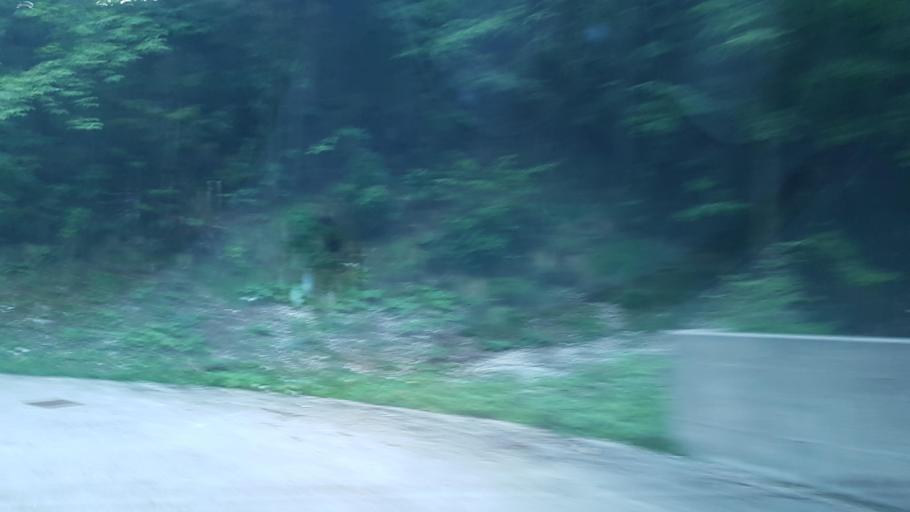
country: IT
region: Friuli Venezia Giulia
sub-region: Provincia di Udine
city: Malborghetto
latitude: 46.3961
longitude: 13.4420
